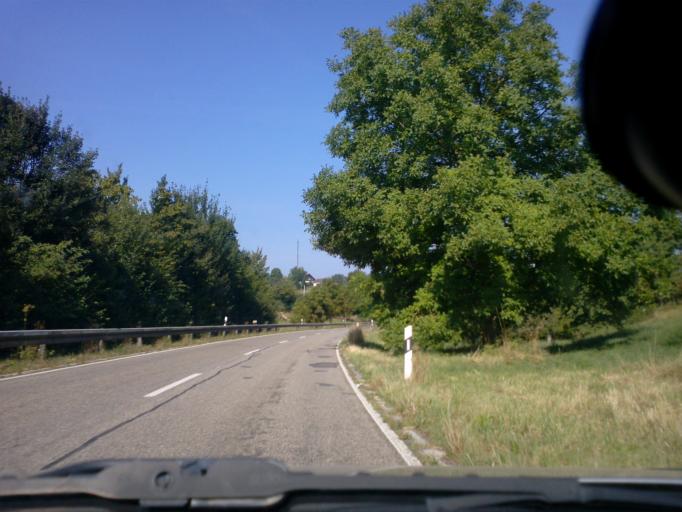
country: DE
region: Baden-Wuerttemberg
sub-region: Karlsruhe Region
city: Joehlingen
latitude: 49.0722
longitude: 8.5939
